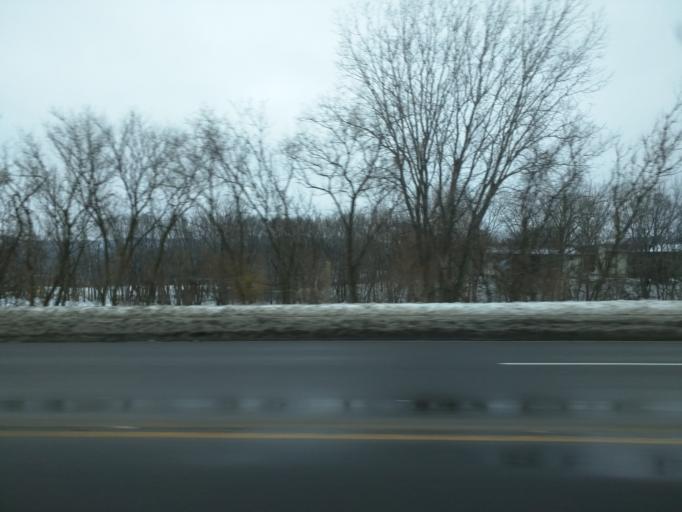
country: US
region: Wisconsin
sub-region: La Crosse County
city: La Crosse
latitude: 43.8190
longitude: -91.2394
